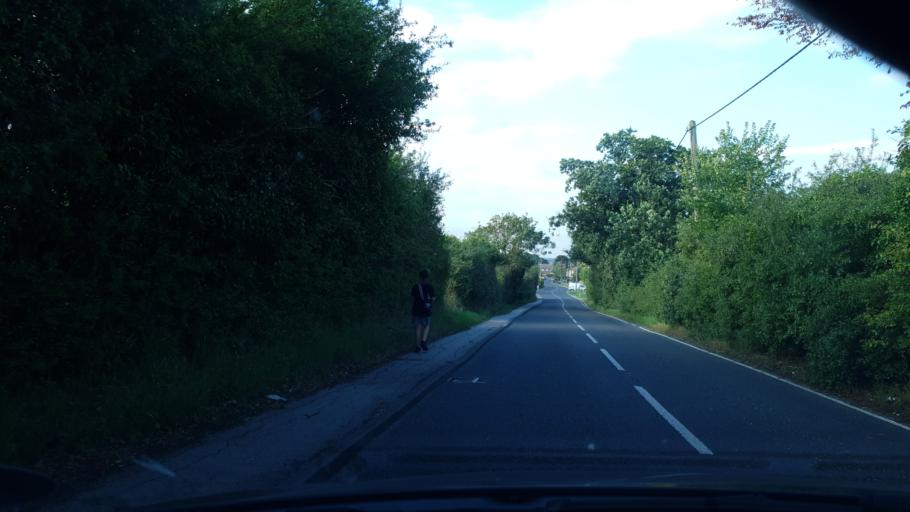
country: GB
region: England
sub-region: Essex
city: Frinton-on-Sea
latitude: 51.8487
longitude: 1.2238
